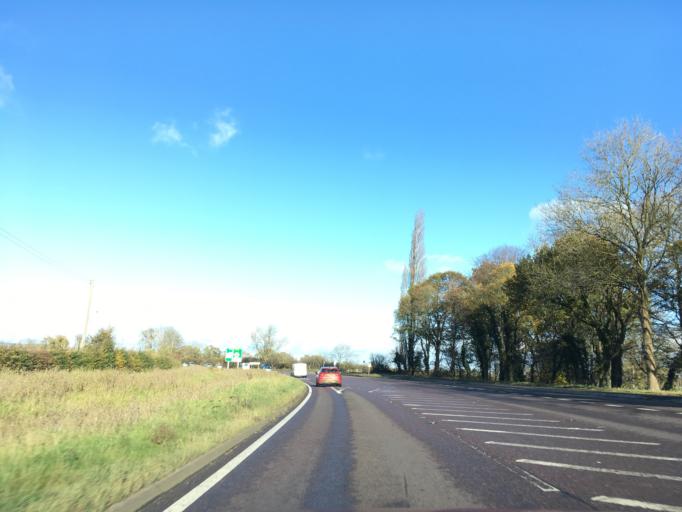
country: GB
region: England
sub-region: Worcestershire
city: Evesham
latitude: 52.0570
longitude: -1.9570
